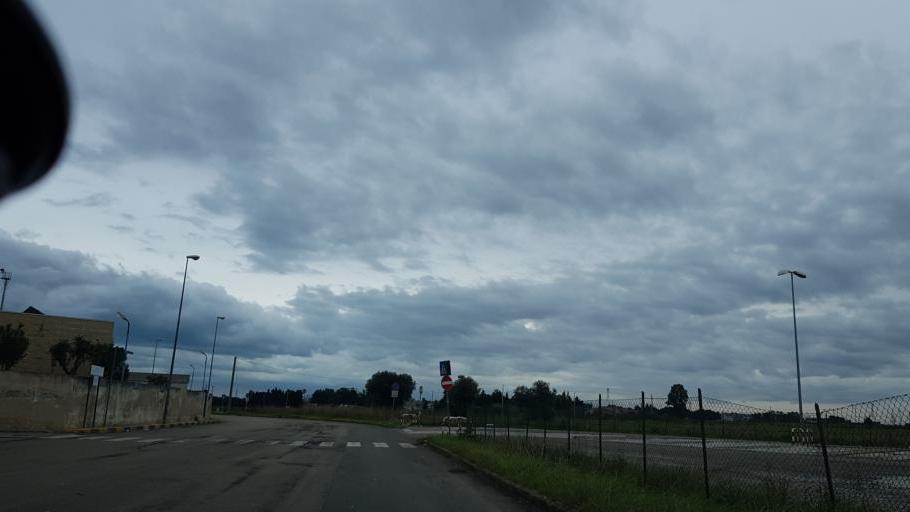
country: IT
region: Apulia
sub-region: Provincia di Brindisi
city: La Rosa
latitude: 40.6138
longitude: 17.9460
